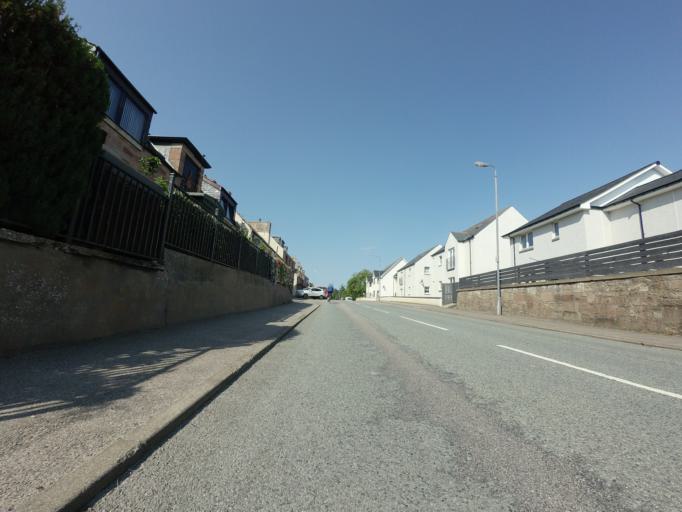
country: GB
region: Scotland
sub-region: Highland
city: Evanton
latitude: 57.6619
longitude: -4.3379
